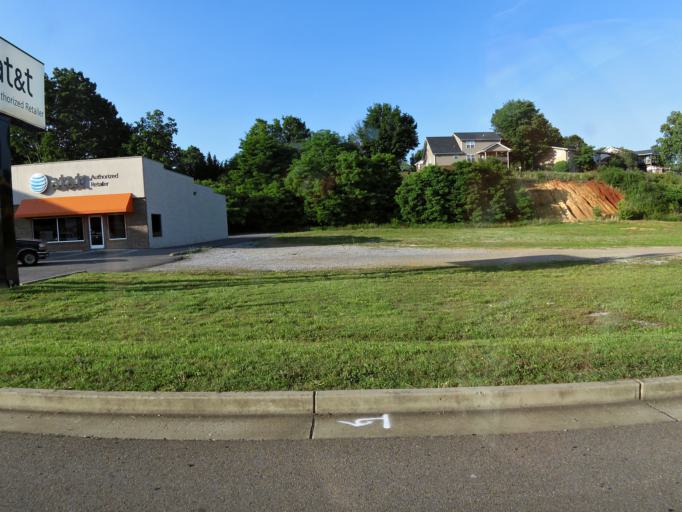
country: US
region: Tennessee
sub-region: Sevier County
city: Seymour
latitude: 35.8691
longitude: -83.7543
